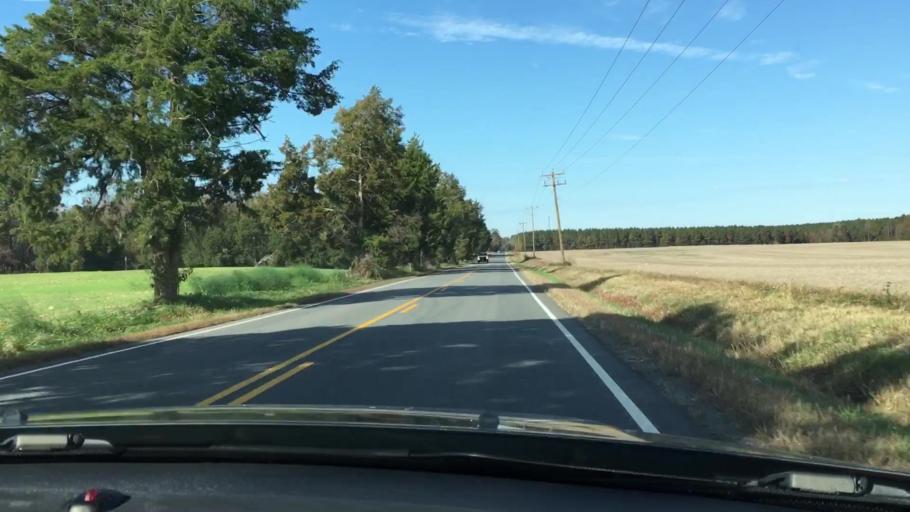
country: US
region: Virginia
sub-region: King and Queen County
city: King and Queen Court House
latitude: 37.6337
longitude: -76.9347
